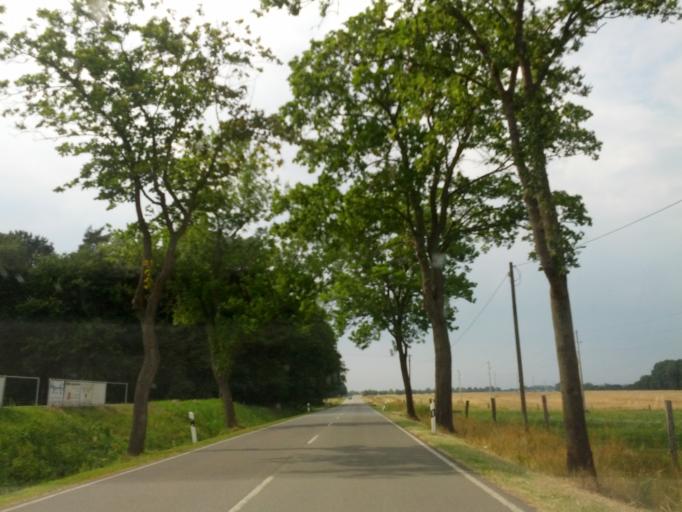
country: DE
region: Brandenburg
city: Fehrbellin
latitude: 52.7624
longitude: 12.8653
